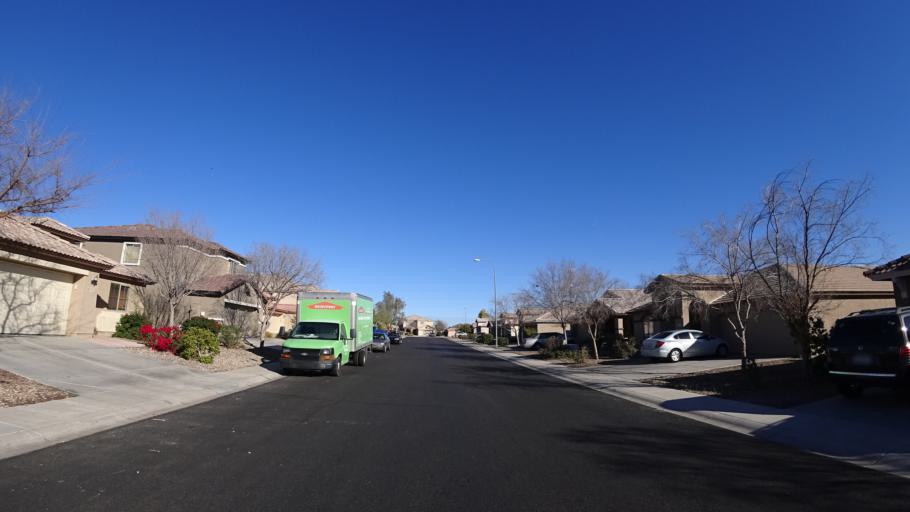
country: US
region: Arizona
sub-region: Maricopa County
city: Avondale
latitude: 33.4348
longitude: -112.3126
